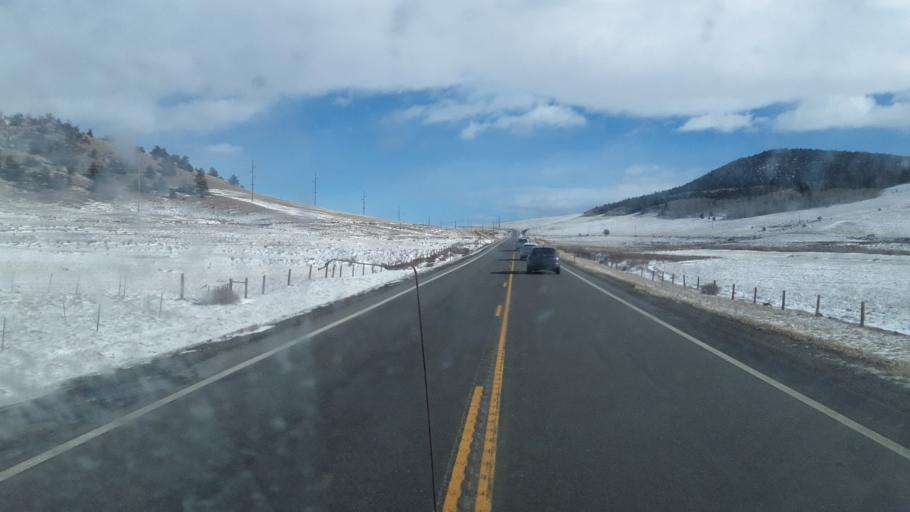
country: US
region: Colorado
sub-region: Park County
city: Fairplay
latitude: 39.2758
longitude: -105.9334
